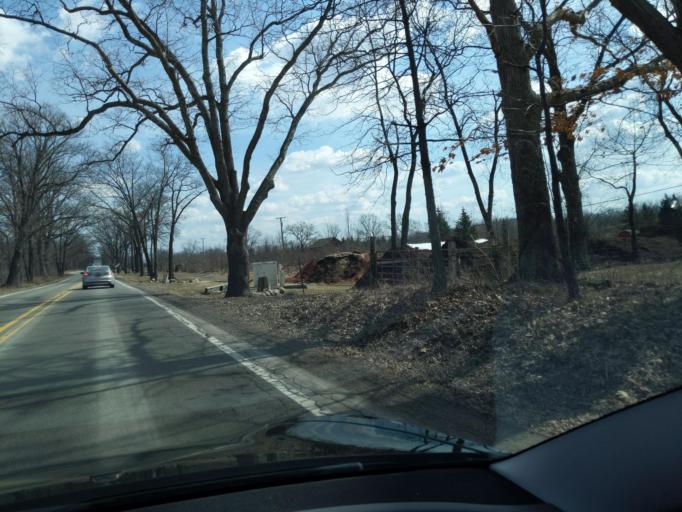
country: US
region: Michigan
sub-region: Washtenaw County
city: Dexter
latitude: 42.3839
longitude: -83.8711
